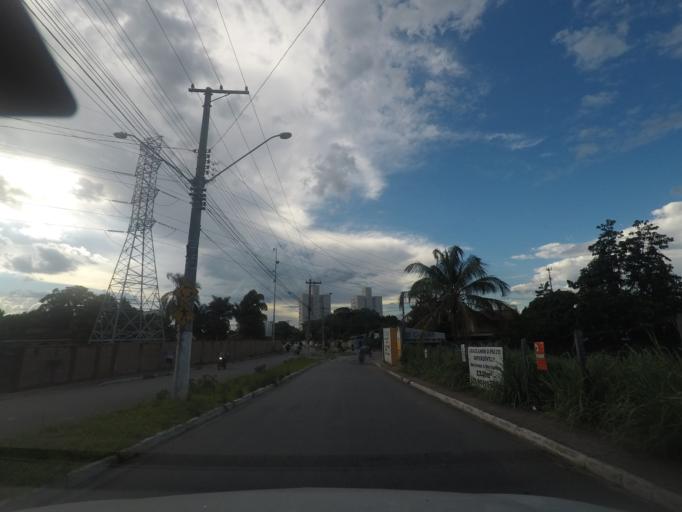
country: BR
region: Sao Paulo
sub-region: Taubate
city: Taubate
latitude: -23.0381
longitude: -45.5914
